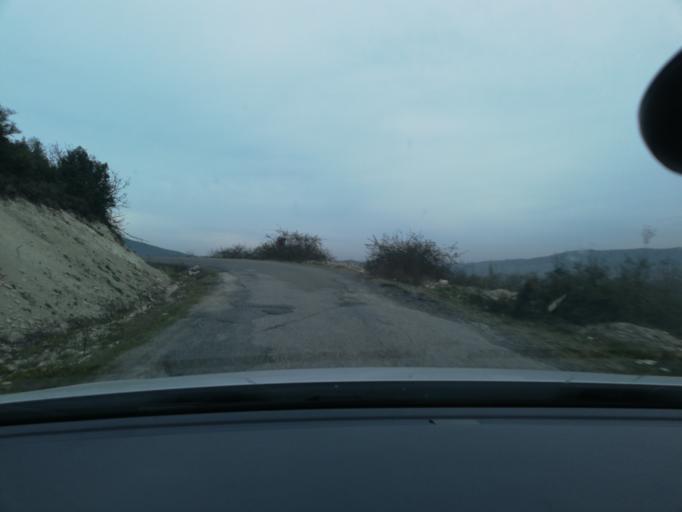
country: TR
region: Zonguldak
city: Saltukova
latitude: 41.5188
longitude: 32.0806
